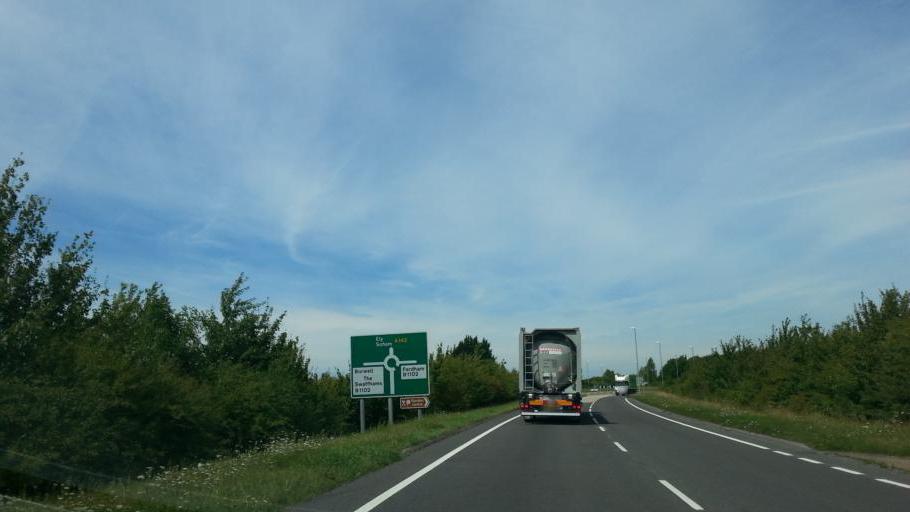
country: GB
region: England
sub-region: Suffolk
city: Exning
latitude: 52.3021
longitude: 0.3741
